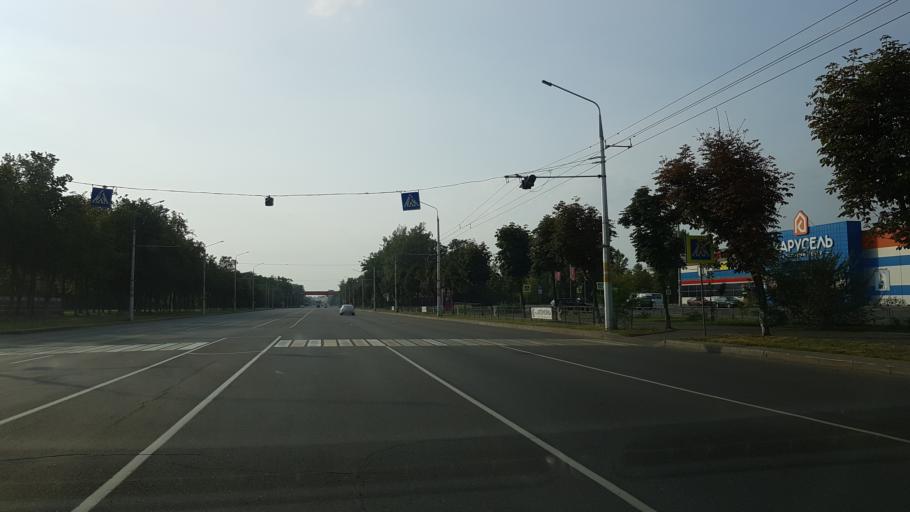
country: BY
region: Mogilev
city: Babruysk
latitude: 53.1709
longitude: 29.2042
